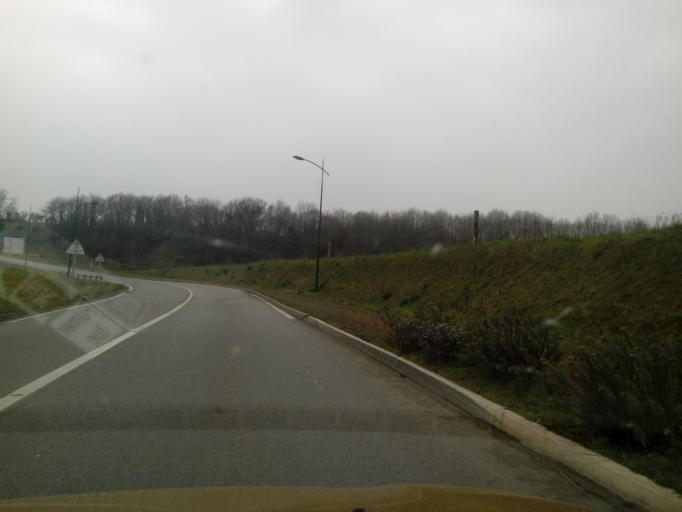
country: FR
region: Brittany
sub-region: Departement du Morbihan
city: Ploermel
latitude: 47.9409
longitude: -2.4057
